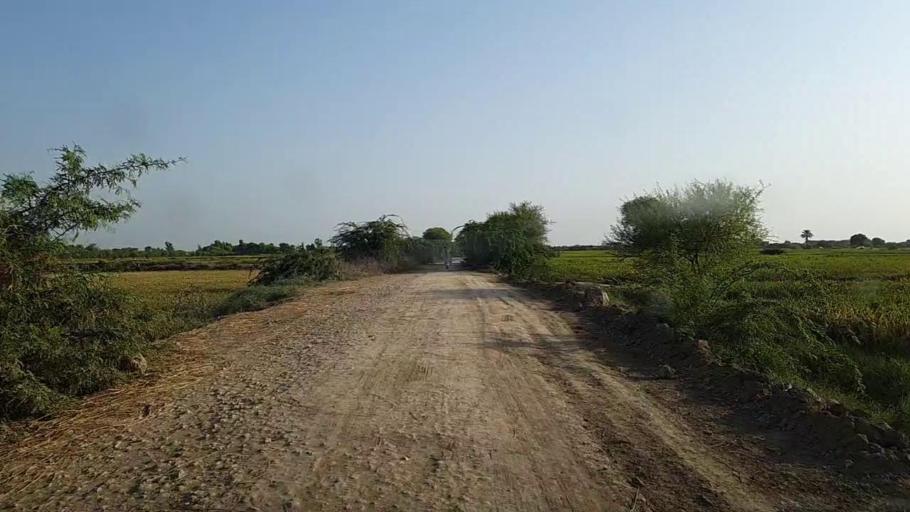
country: PK
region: Sindh
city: Bulri
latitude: 24.7484
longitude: 68.4219
